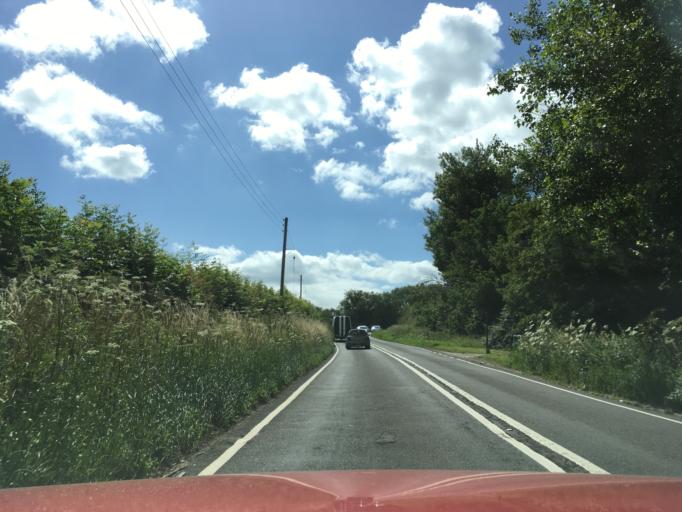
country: GB
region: England
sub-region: Buckinghamshire
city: Winslow
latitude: 51.8975
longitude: -0.8316
